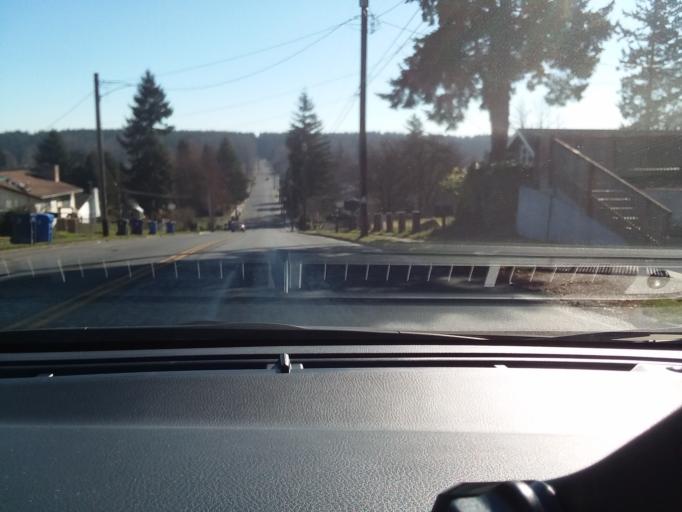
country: US
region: Washington
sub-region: Pierce County
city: Midland
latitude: 47.2063
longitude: -122.4146
